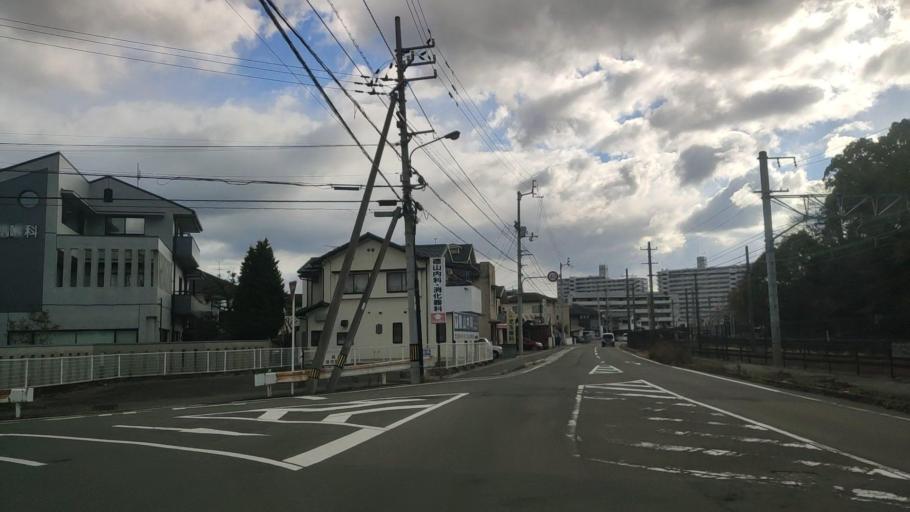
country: JP
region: Ehime
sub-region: Shikoku-chuo Shi
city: Matsuyama
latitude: 33.8697
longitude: 132.7159
